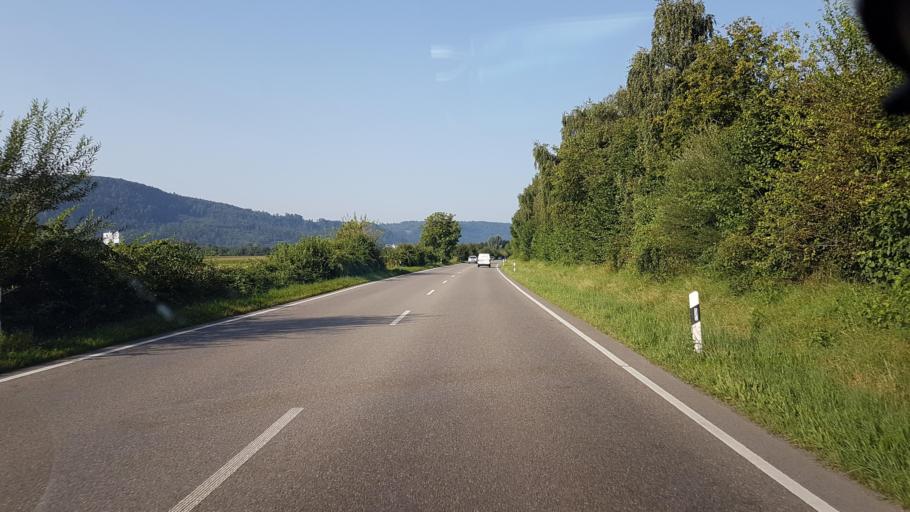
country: DE
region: Baden-Wuerttemberg
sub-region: Freiburg Region
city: Dogern
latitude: 47.6060
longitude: 8.1717
